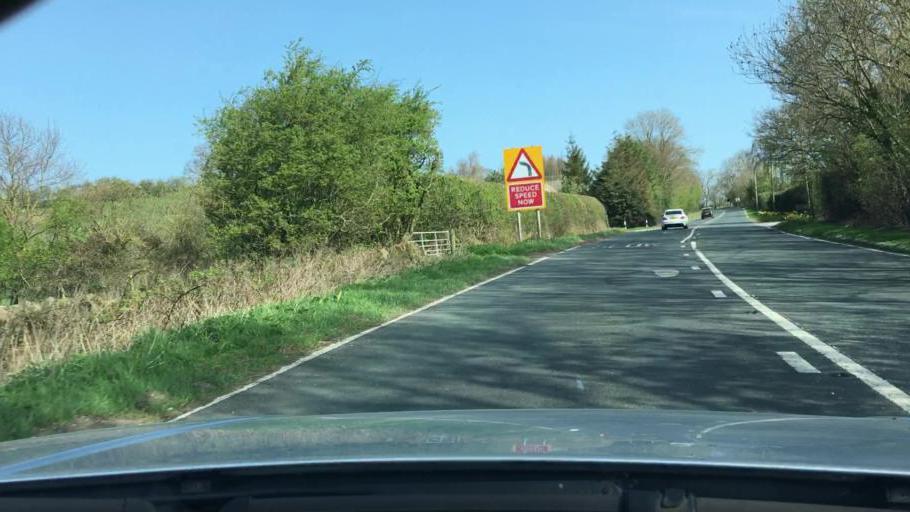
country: GB
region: England
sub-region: North Yorkshire
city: Pannal
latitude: 53.9370
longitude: -1.5368
